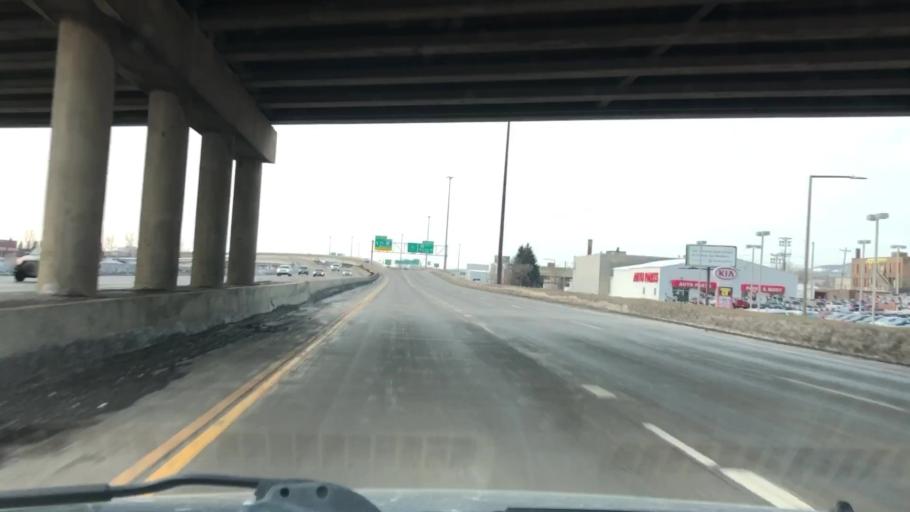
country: US
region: Minnesota
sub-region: Saint Louis County
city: Duluth
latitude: 46.7704
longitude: -92.1173
